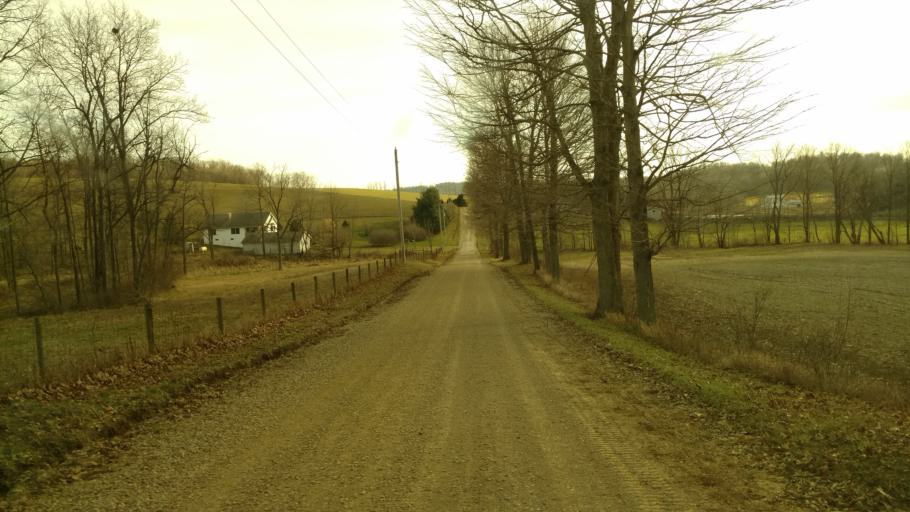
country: US
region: Ohio
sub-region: Ashland County
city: Loudonville
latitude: 40.5595
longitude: -82.3266
